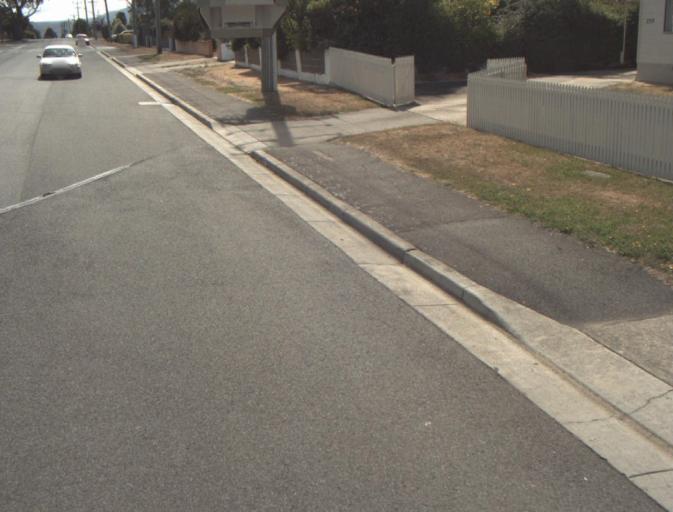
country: AU
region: Tasmania
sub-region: Launceston
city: Summerhill
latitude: -41.4705
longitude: 147.1216
